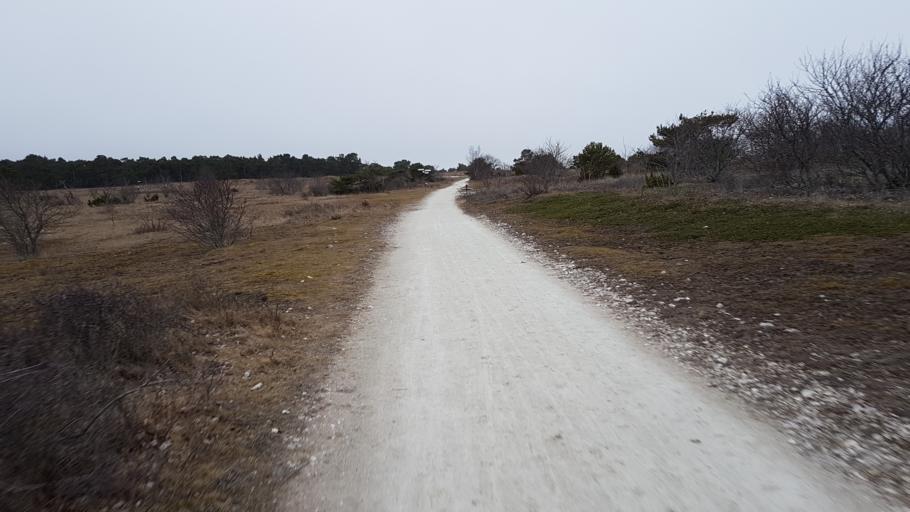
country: SE
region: Gotland
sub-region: Gotland
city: Vibble
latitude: 57.6195
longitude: 18.2654
